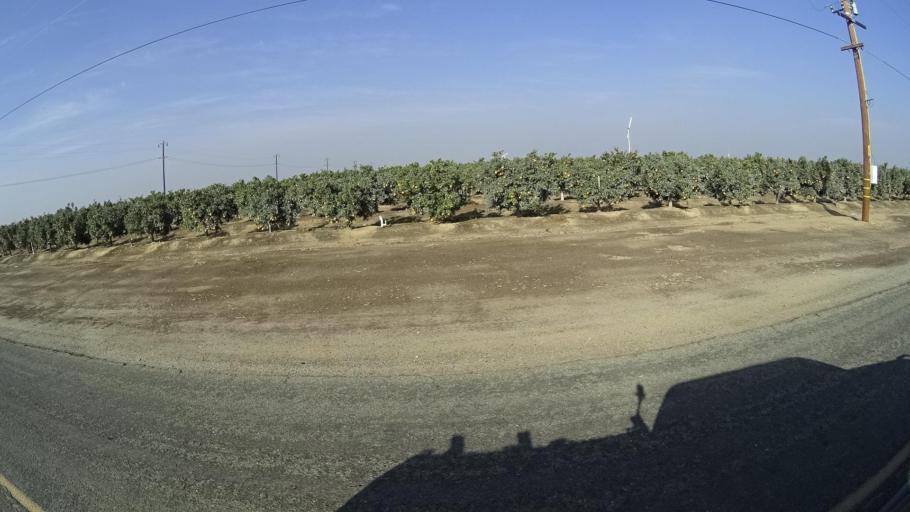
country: US
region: California
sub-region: Tulare County
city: Richgrove
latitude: 35.7907
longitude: -119.0884
